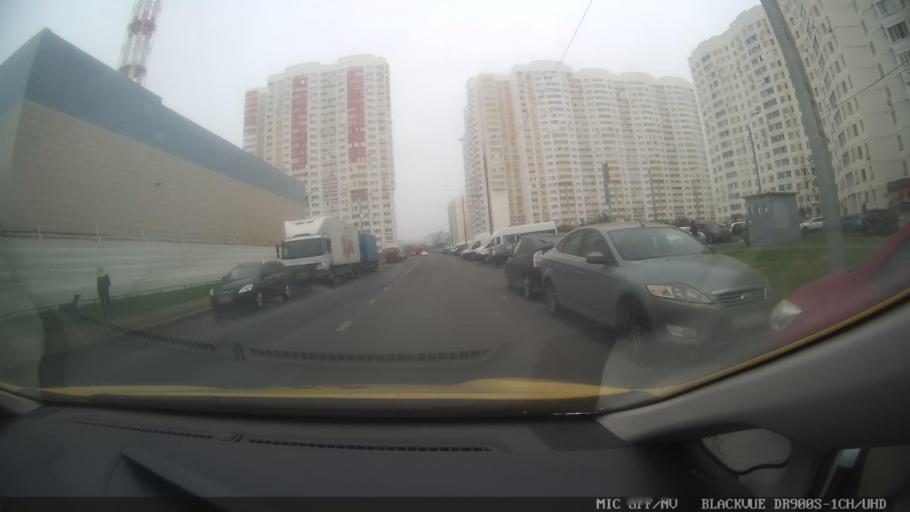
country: RU
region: Moscow
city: Nekrasovka
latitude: 55.6861
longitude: 37.9087
